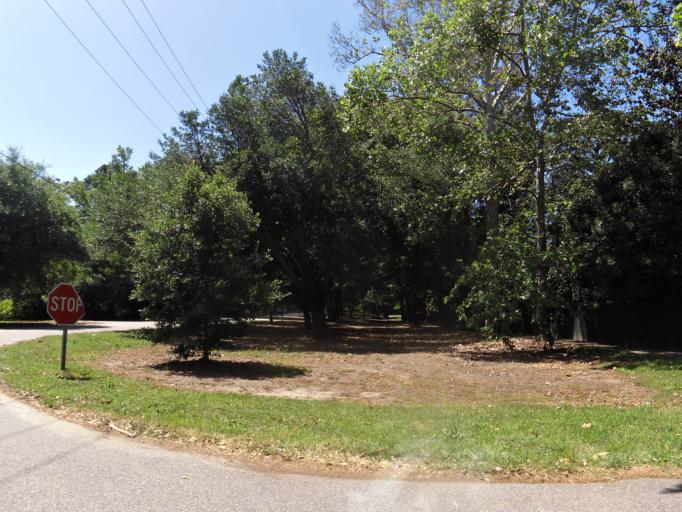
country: US
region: South Carolina
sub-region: Aiken County
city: Aiken
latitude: 33.5535
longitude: -81.7181
